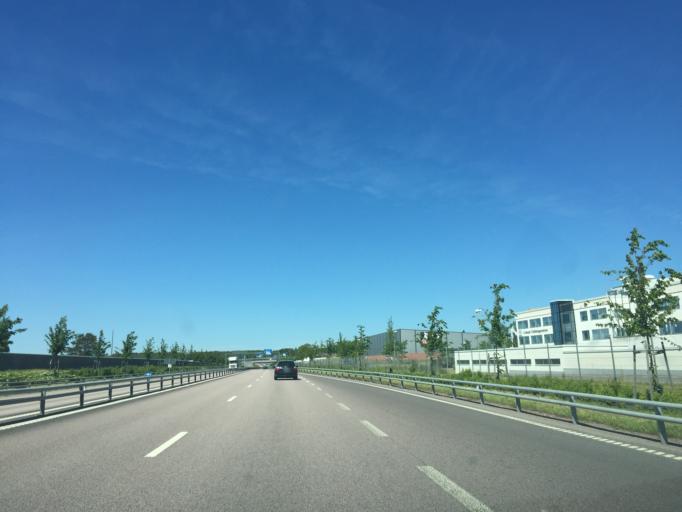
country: SE
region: OEstergoetland
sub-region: Motala Kommun
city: Motala
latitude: 58.5487
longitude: 15.0150
